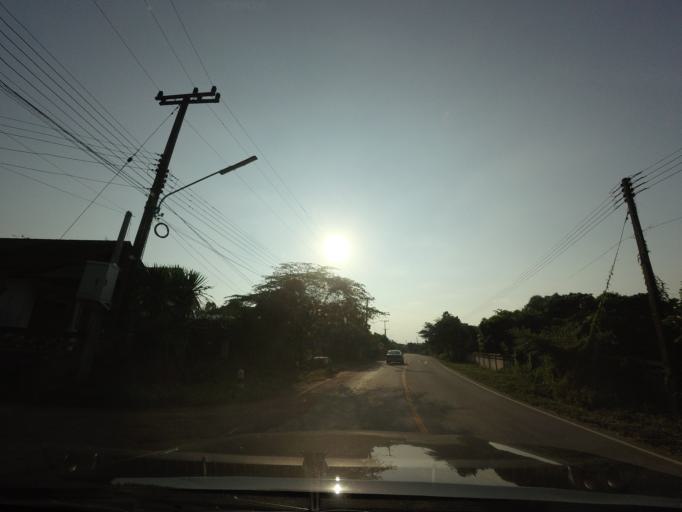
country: TH
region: Nan
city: Na Noi
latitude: 18.3344
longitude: 100.7686
